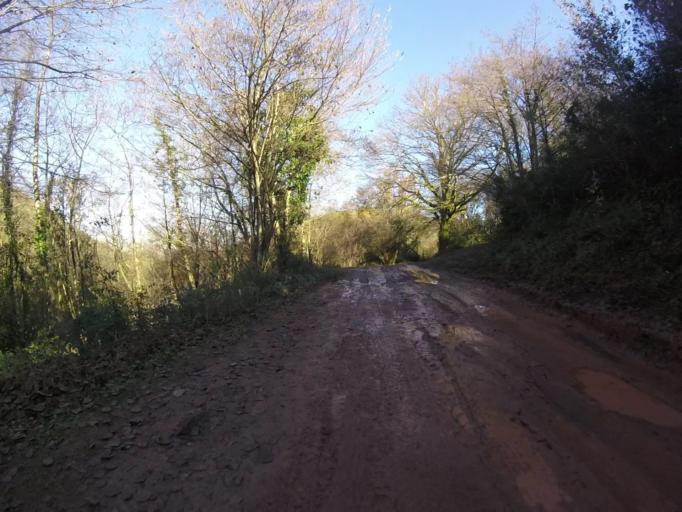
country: ES
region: Navarre
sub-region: Provincia de Navarra
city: Bera
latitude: 43.3189
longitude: -1.7090
